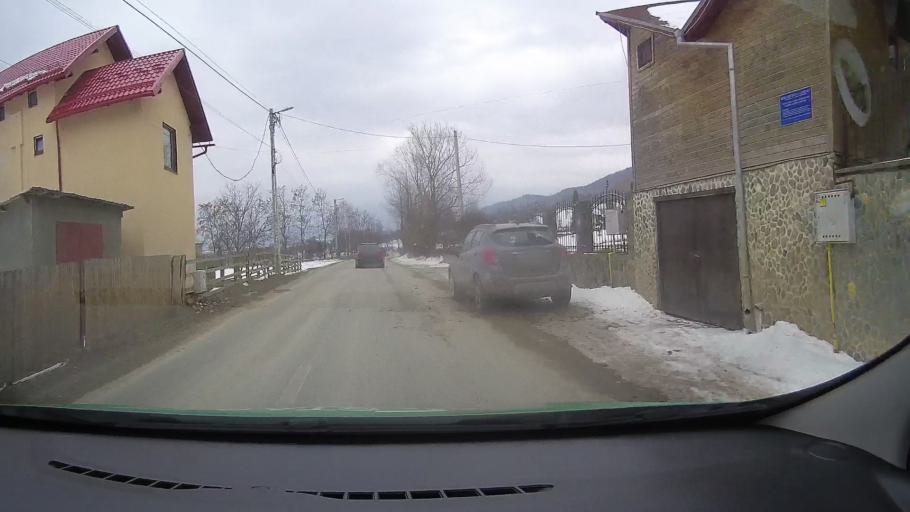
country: RO
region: Brasov
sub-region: Comuna Zarnesti
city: Zarnesti
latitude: 45.5397
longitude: 25.3318
